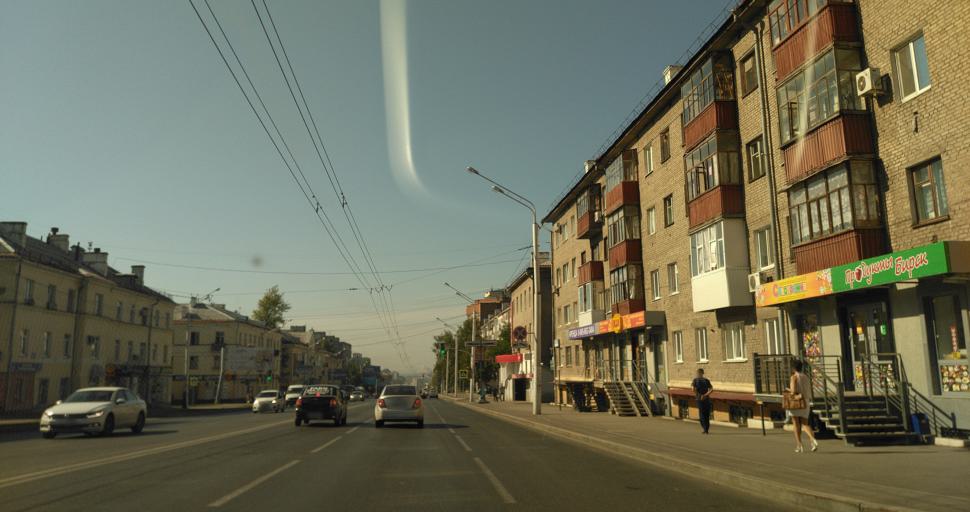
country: RU
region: Bashkortostan
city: Ufa
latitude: 54.7341
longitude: 55.9798
